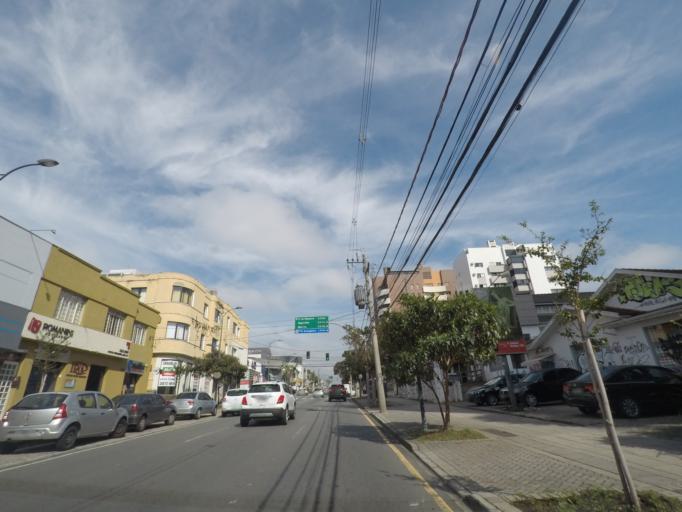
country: BR
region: Parana
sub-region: Curitiba
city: Curitiba
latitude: -25.4367
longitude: -49.2894
